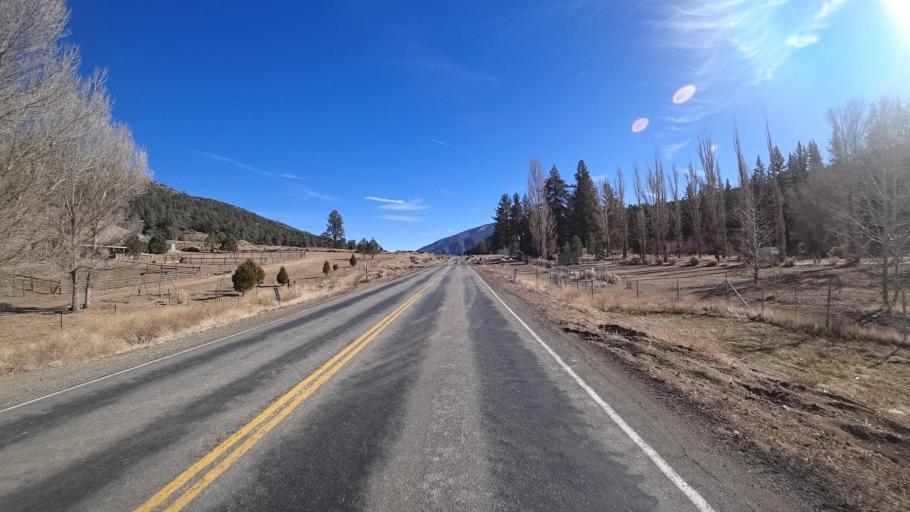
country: US
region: California
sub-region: Kern County
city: Frazier Park
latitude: 34.8287
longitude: -119.0237
